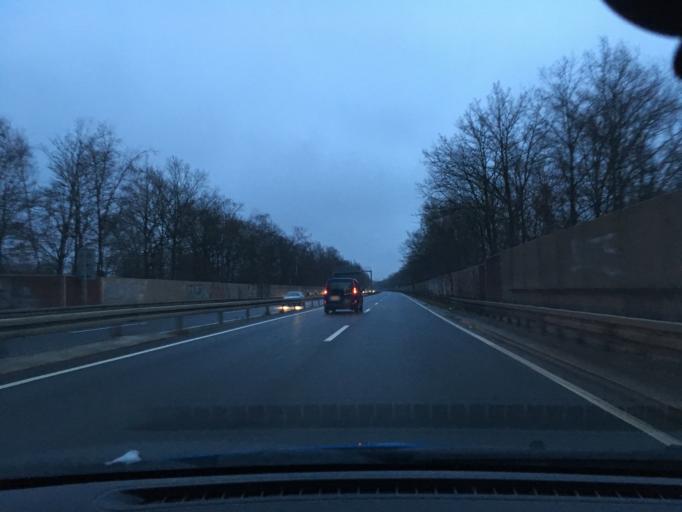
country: DE
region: Lower Saxony
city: Laatzen
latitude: 52.3551
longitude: 9.8341
